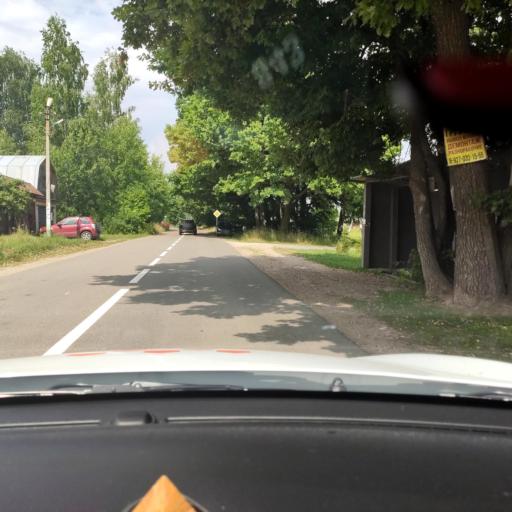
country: RU
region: Tatarstan
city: Osinovo
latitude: 55.9054
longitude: 48.9627
